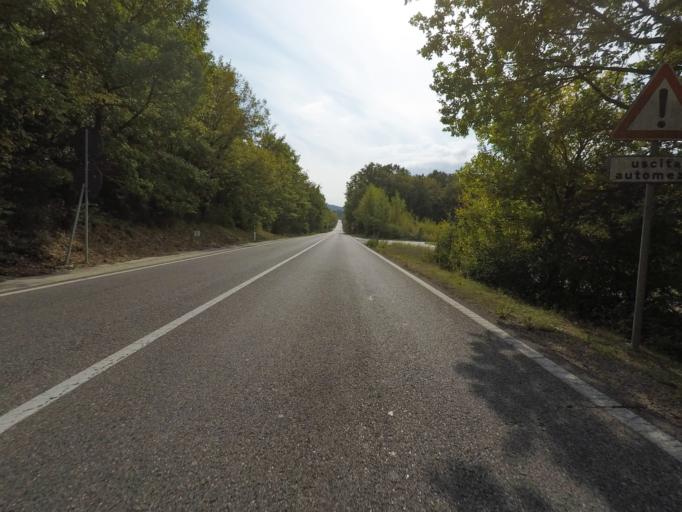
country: IT
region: Tuscany
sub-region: Provincia di Siena
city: Rosia
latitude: 43.1783
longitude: 11.2776
